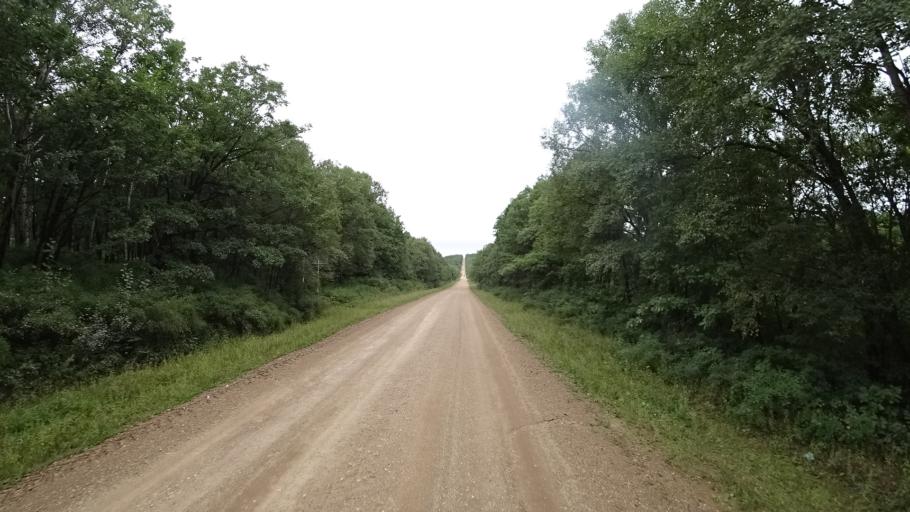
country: RU
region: Primorskiy
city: Ivanovka
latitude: 44.0199
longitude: 132.5195
